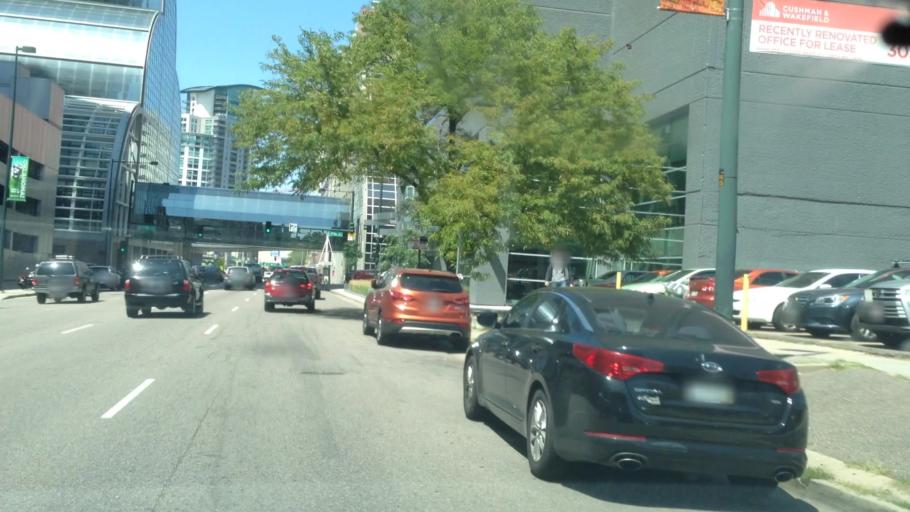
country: US
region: Colorado
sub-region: Denver County
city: Denver
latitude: 39.7424
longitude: -104.9861
